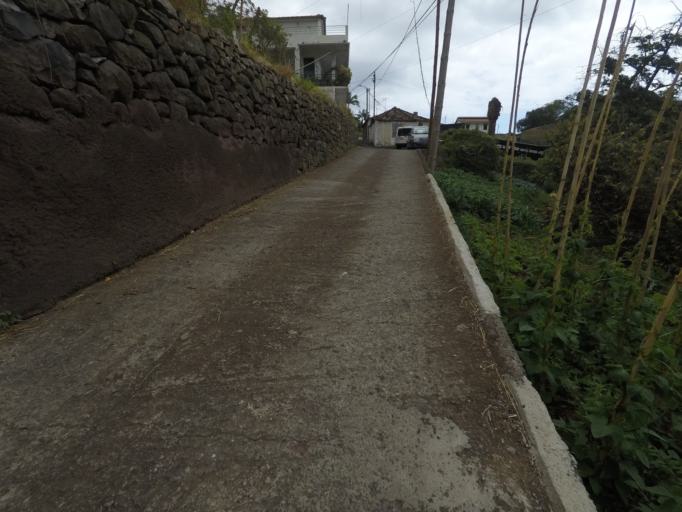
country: PT
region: Madeira
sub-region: Santana
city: Santana
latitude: 32.7671
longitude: -16.8316
